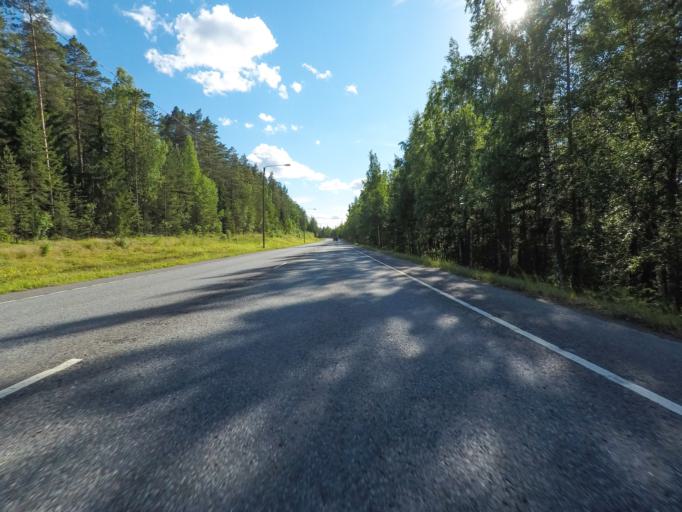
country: FI
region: Uusimaa
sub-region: Helsinki
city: Vihti
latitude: 60.3389
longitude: 24.2978
